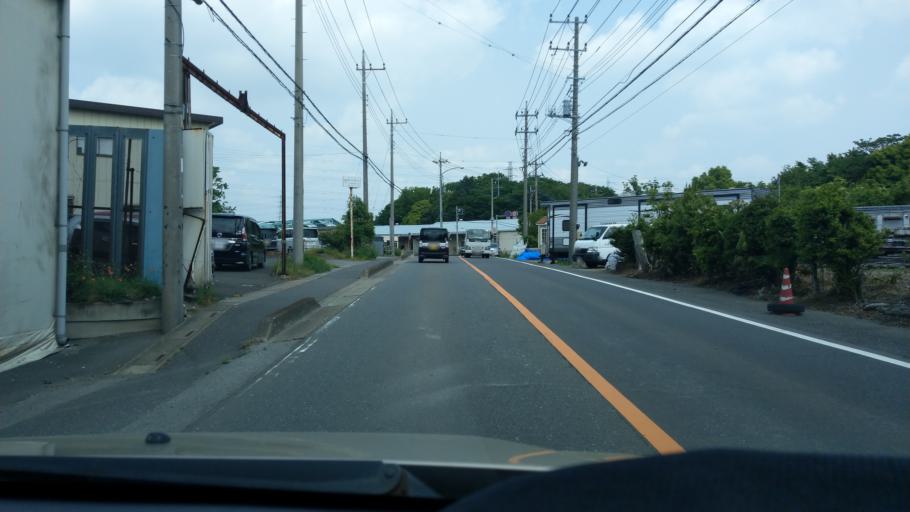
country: JP
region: Saitama
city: Iwatsuki
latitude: 35.9175
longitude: 139.7164
